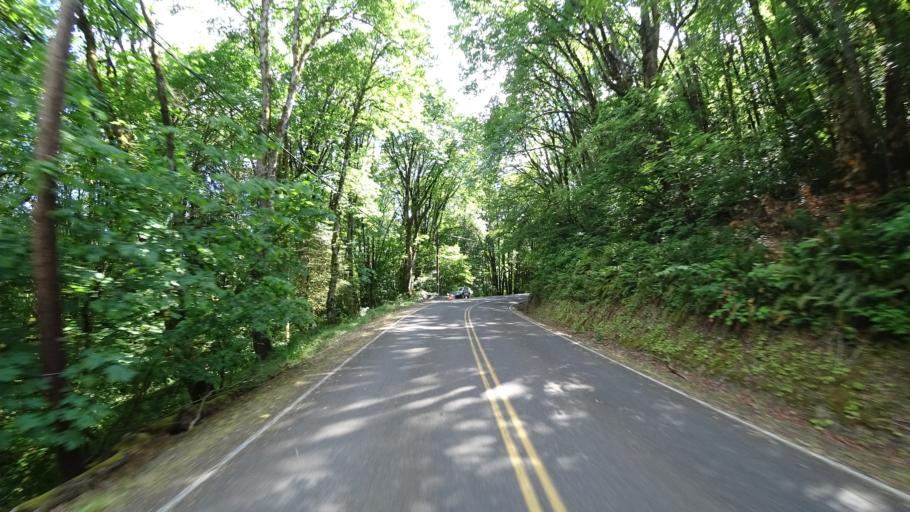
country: US
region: Oregon
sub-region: Washington County
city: Bethany
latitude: 45.6060
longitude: -122.8232
